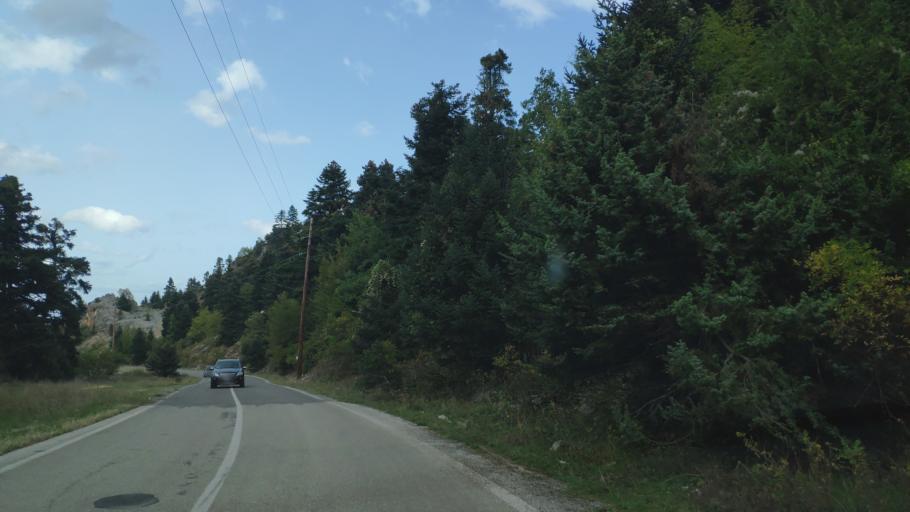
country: GR
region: Central Greece
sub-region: Nomos Fthiotidos
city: Anthili
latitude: 38.7329
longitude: 22.3677
